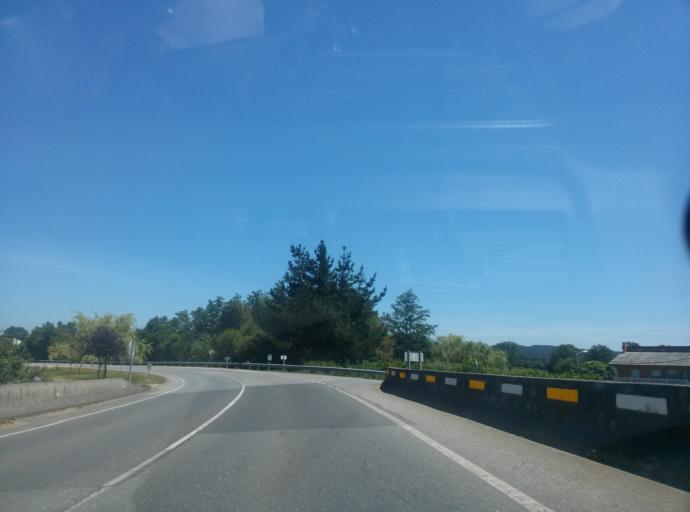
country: ES
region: Galicia
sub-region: Provincia de Lugo
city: Mos
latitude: 43.1817
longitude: -7.4761
